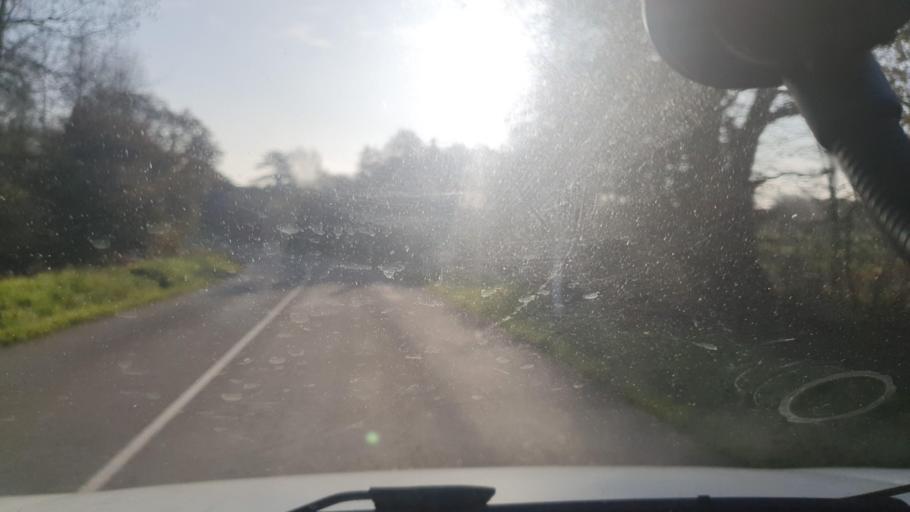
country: FR
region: Brittany
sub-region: Departement du Finistere
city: Briec
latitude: 48.0930
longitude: -4.0033
